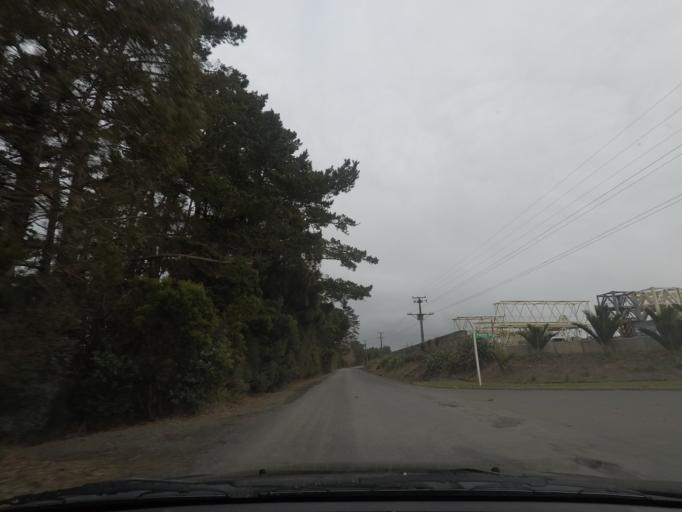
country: NZ
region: Auckland
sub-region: Auckland
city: Muriwai Beach
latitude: -36.7584
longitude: 174.5754
